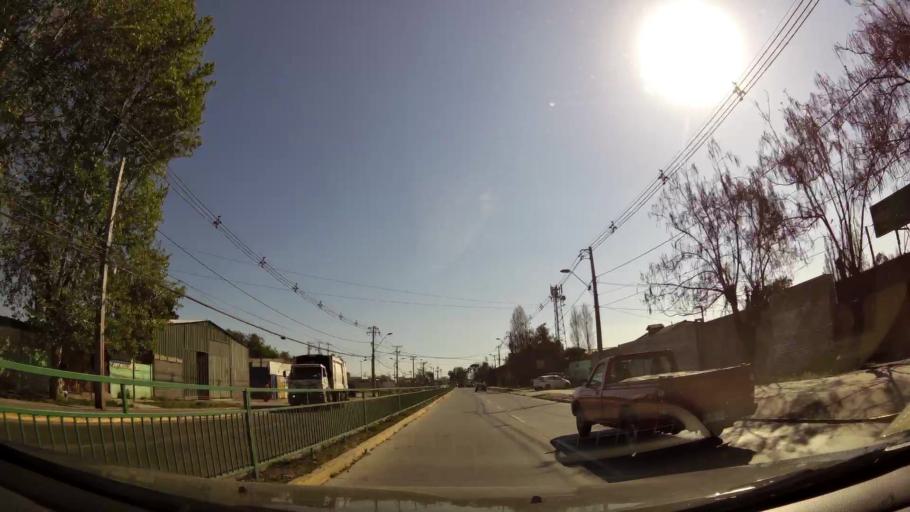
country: CL
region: Santiago Metropolitan
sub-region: Provincia de Santiago
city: La Pintana
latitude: -33.5853
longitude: -70.6259
